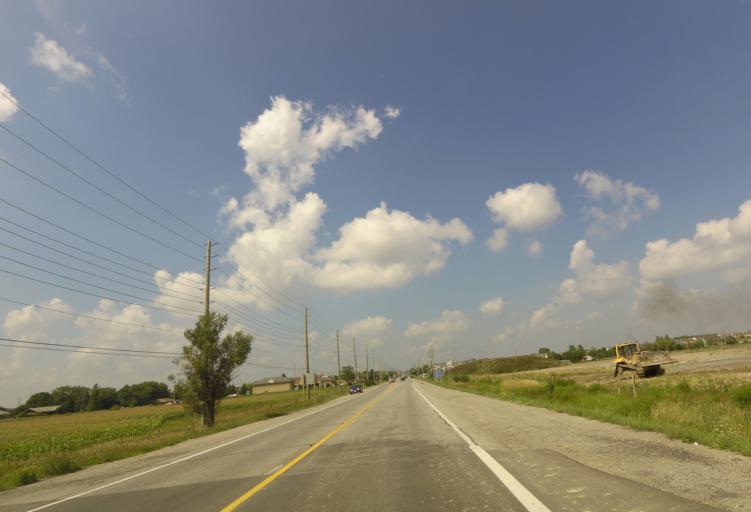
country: CA
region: Ontario
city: Oshawa
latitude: 43.9542
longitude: -78.9421
